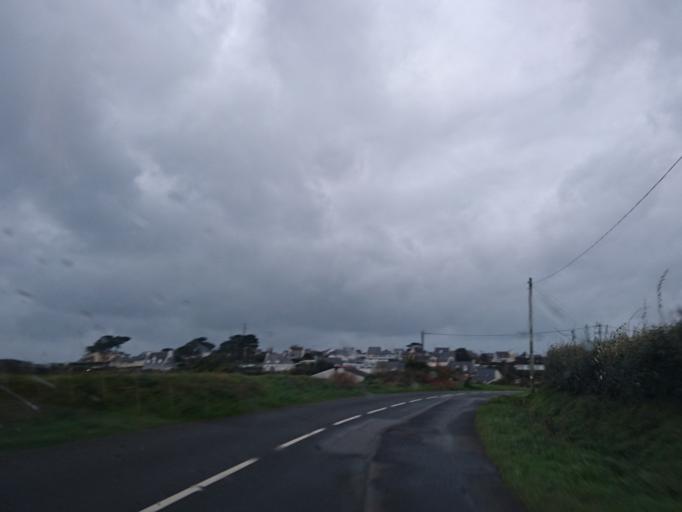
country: FR
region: Brittany
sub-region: Departement du Finistere
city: Le Conquet
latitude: 48.3508
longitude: -4.7730
